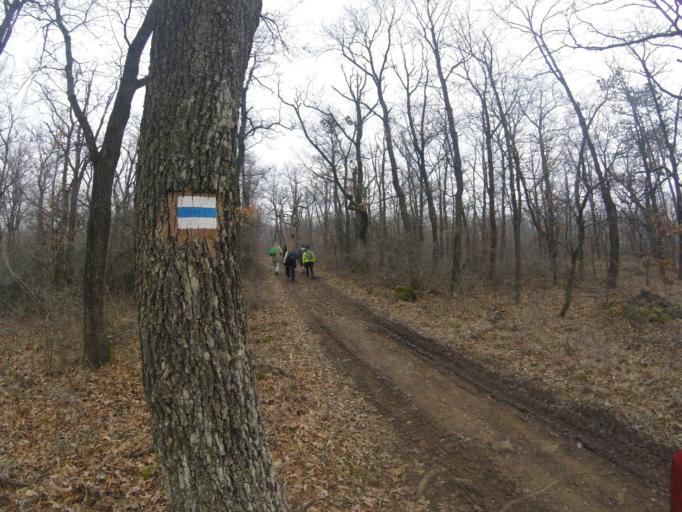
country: HU
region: Nograd
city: Paszto
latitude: 47.9376
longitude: 19.6318
